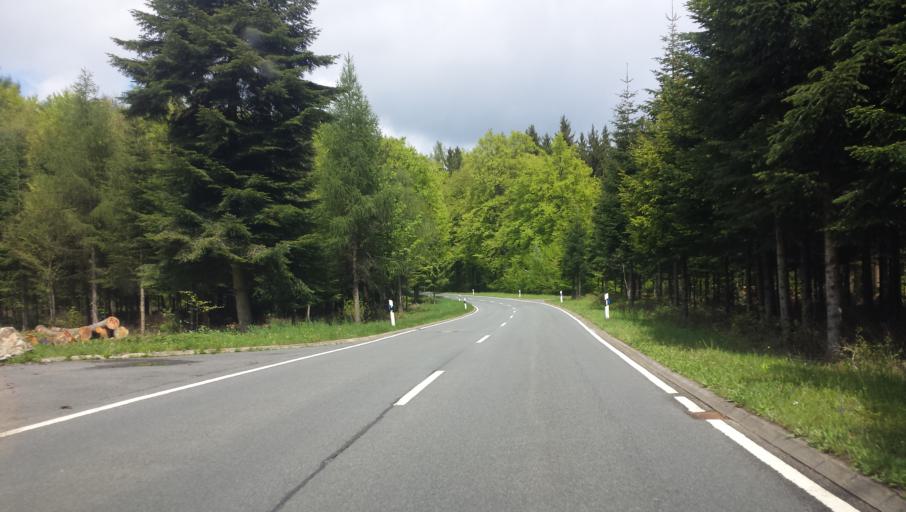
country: DE
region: Baden-Wuerttemberg
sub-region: Karlsruhe Region
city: Fahrenbach
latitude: 49.4338
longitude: 9.1030
